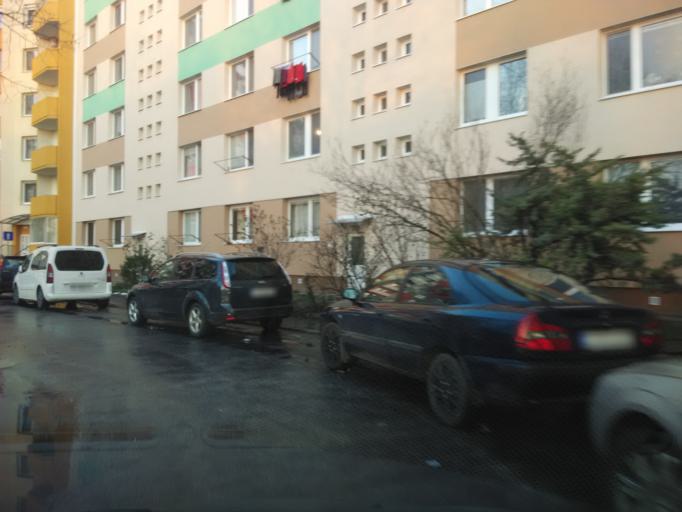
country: SK
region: Trnavsky
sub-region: Okres Trnava
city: Trnava
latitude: 48.3808
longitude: 17.5786
